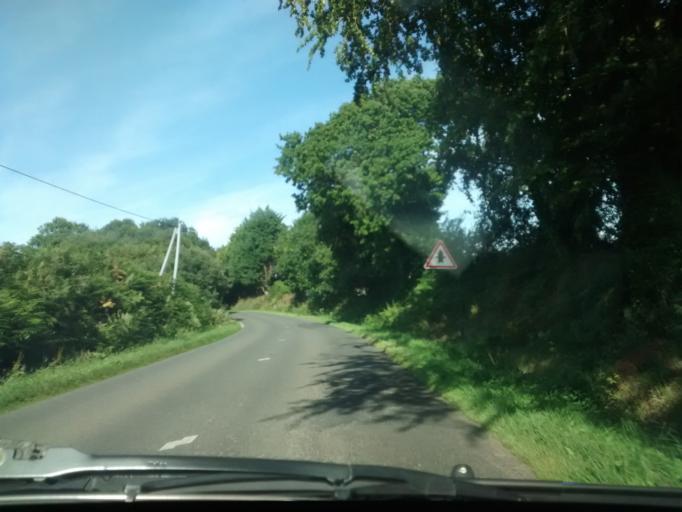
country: FR
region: Brittany
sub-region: Departement des Cotes-d'Armor
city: Rospez
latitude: 48.7551
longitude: -3.4045
